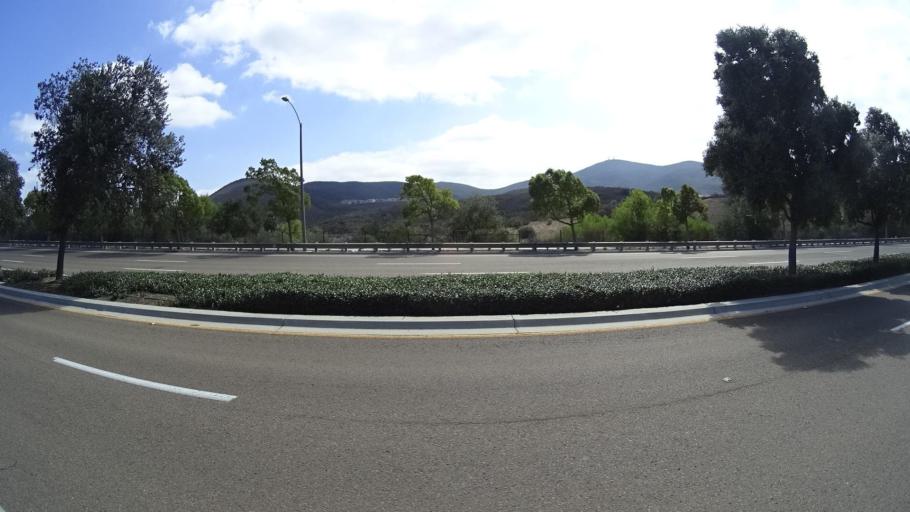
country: US
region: California
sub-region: San Diego County
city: Poway
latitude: 33.0024
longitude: -117.1023
